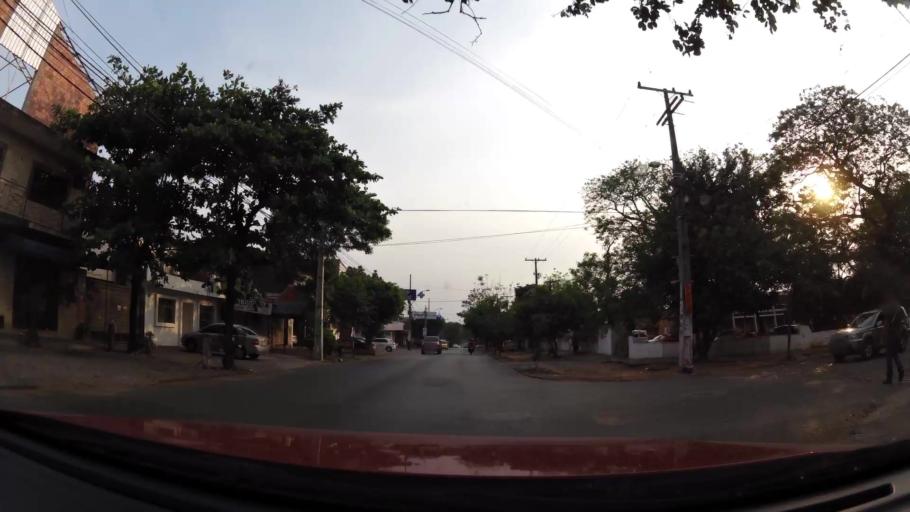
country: PY
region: Central
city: Lambare
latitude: -25.3196
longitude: -57.5769
